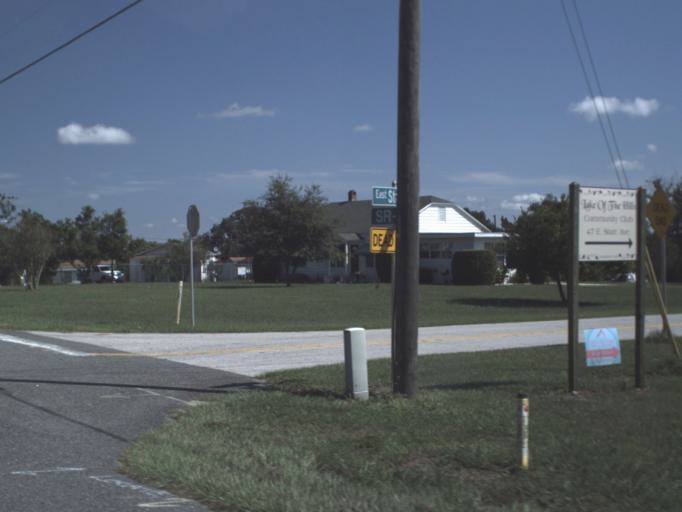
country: US
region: Florida
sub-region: Polk County
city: Lake Wales
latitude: 27.9552
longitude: -81.5947
